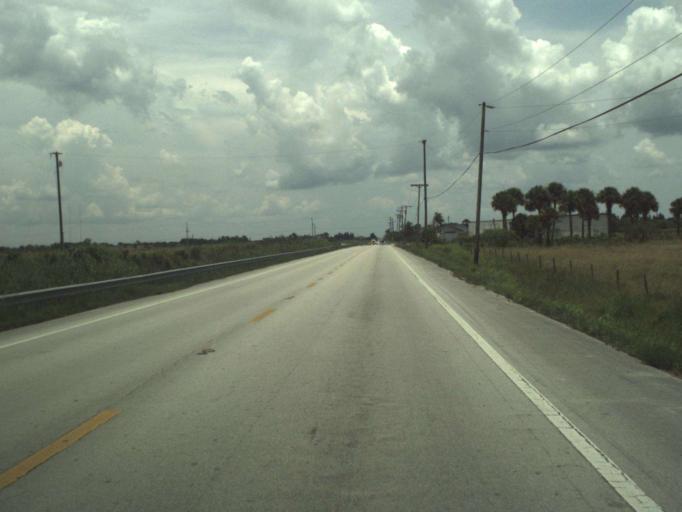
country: US
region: Florida
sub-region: Saint Lucie County
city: Fort Pierce South
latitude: 27.4208
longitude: -80.3991
